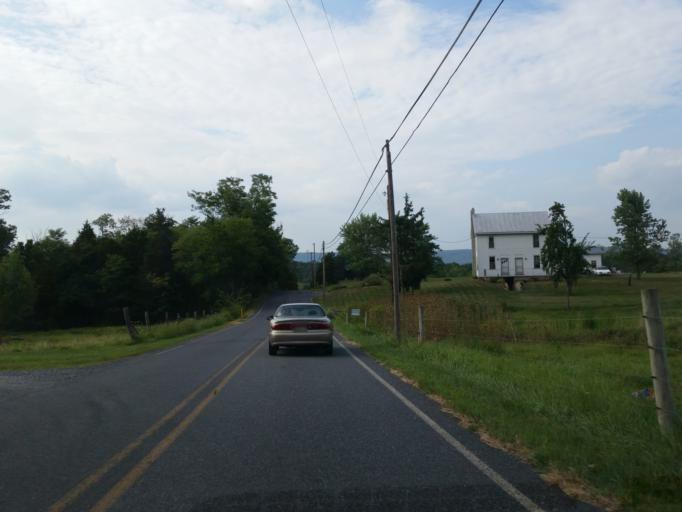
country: US
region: Pennsylvania
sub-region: Lebanon County
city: Jonestown
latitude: 40.4081
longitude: -76.5366
